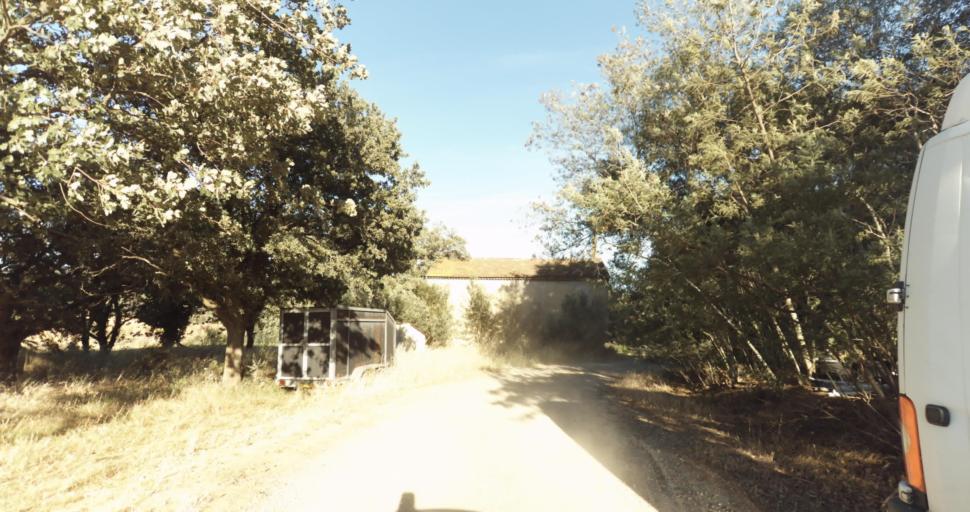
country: FR
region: Provence-Alpes-Cote d'Azur
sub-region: Departement du Var
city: La Croix-Valmer
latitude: 43.2164
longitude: 6.5658
